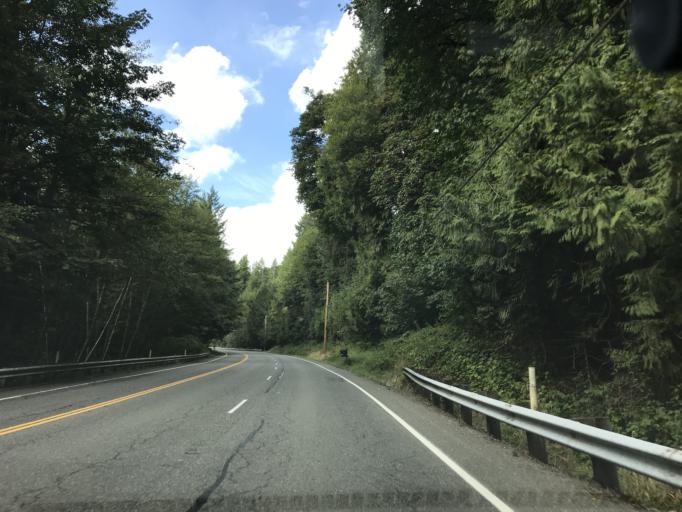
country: US
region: Washington
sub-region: King County
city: Black Diamond
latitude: 47.2882
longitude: -122.0506
